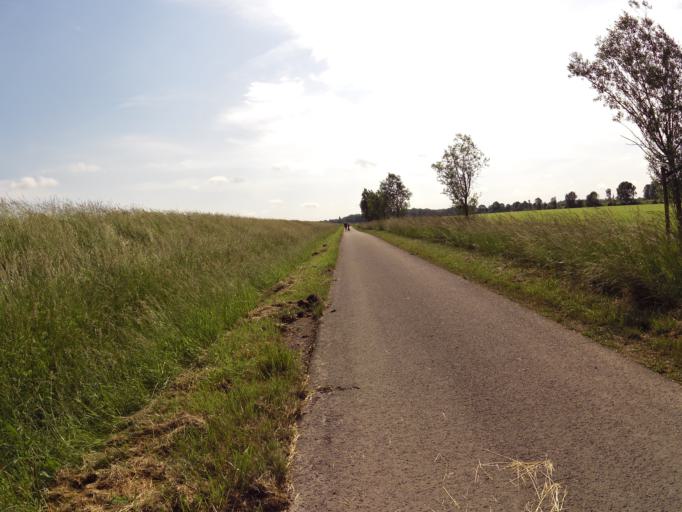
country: FR
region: Champagne-Ardenne
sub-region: Departement de l'Aube
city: Saint-Julien-les-Villas
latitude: 48.2650
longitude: 4.1170
